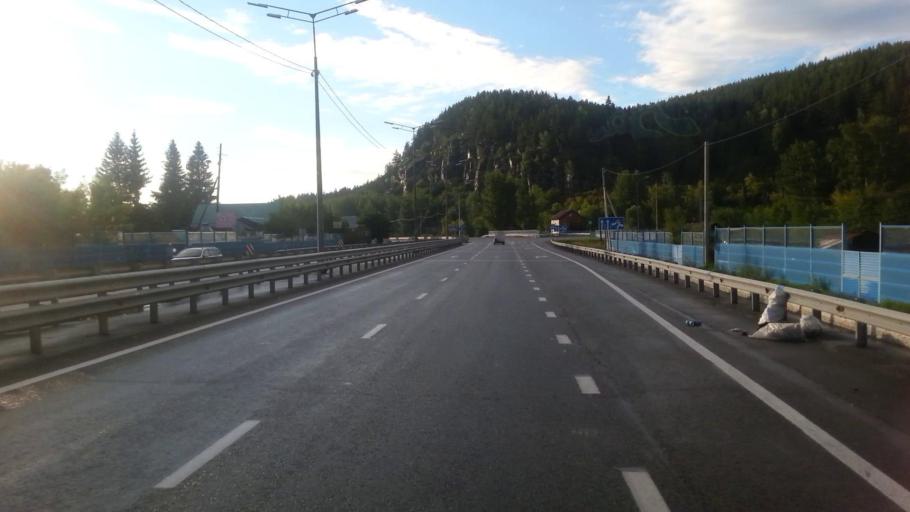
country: RU
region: Altay
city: Souzga
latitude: 51.9169
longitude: 85.8604
